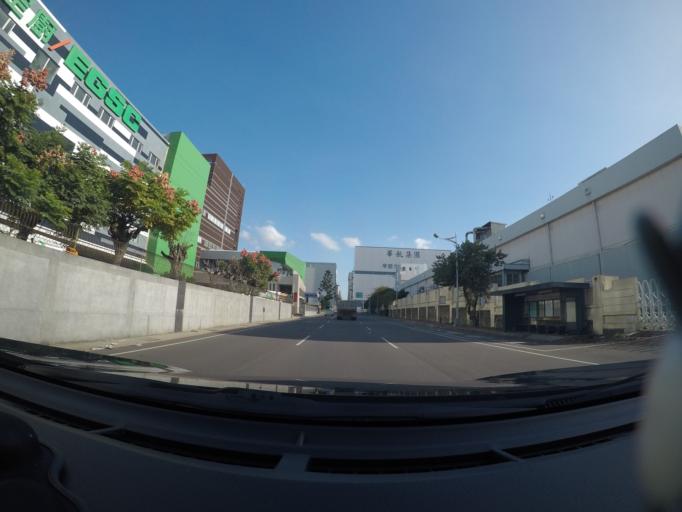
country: TW
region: Taiwan
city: Taoyuan City
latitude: 25.0899
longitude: 121.2483
